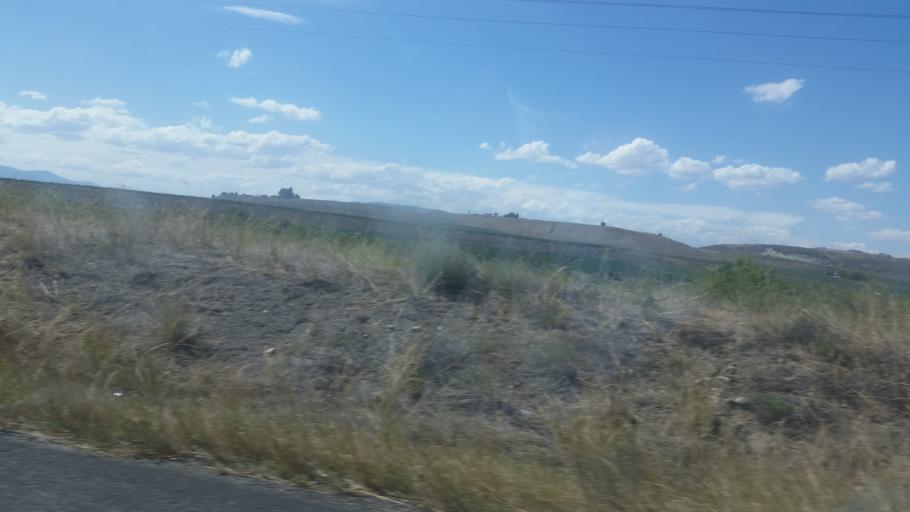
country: US
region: Washington
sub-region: Okanogan County
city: Brewster
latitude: 48.1242
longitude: -119.6742
